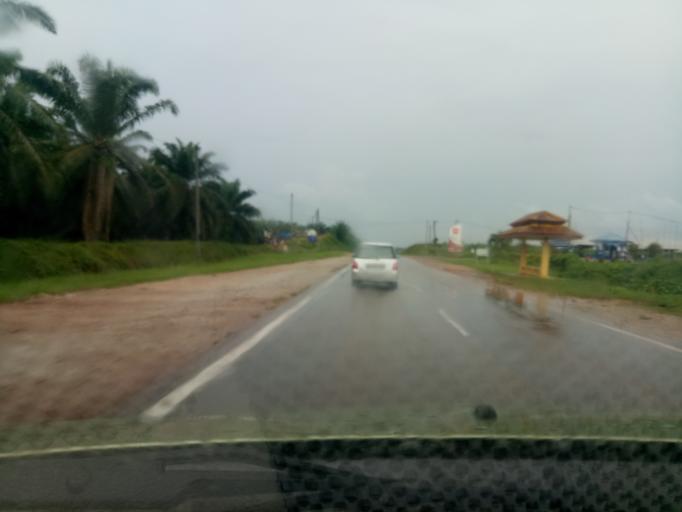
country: MY
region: Kedah
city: Sungai Petani
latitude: 5.5722
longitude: 100.5778
